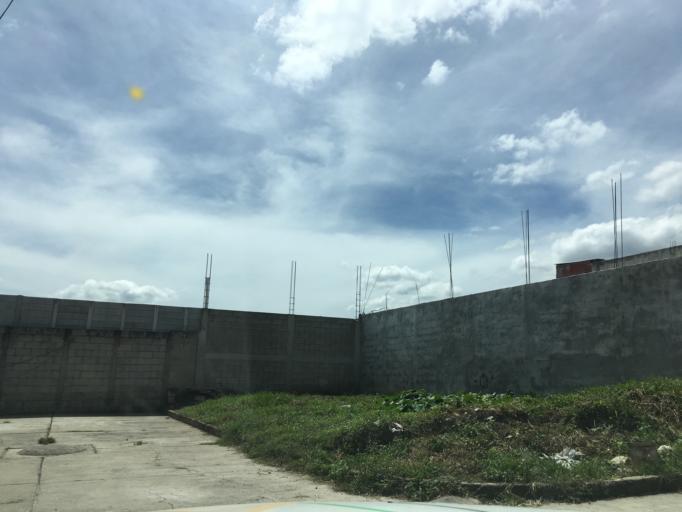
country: GT
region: Guatemala
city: Petapa
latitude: 14.5036
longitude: -90.5696
